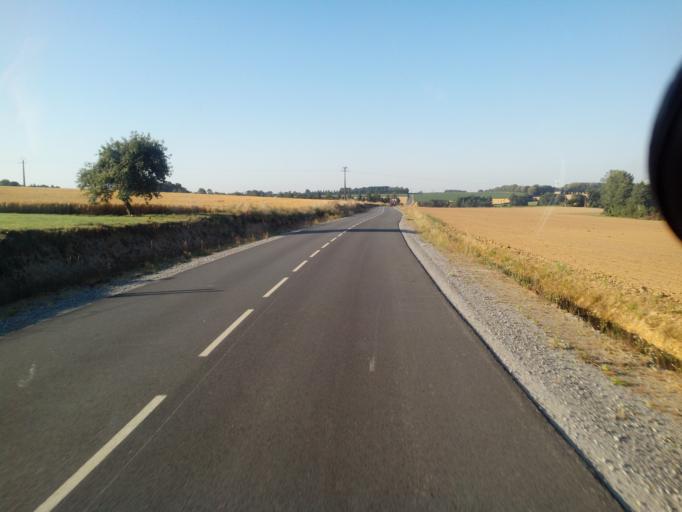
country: FR
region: Brittany
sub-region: Departement du Morbihan
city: Meneac
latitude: 48.1251
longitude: -2.4593
